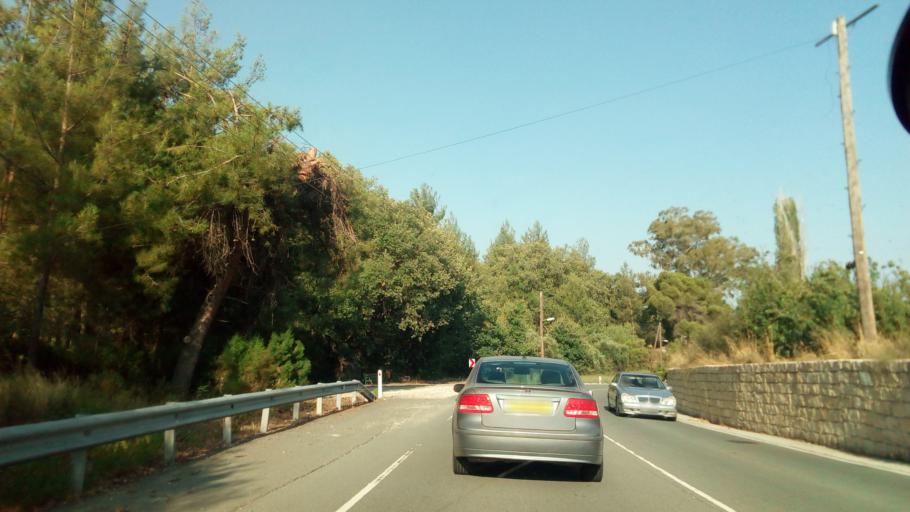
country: CY
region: Limassol
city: Pelendri
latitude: 34.8625
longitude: 32.8671
